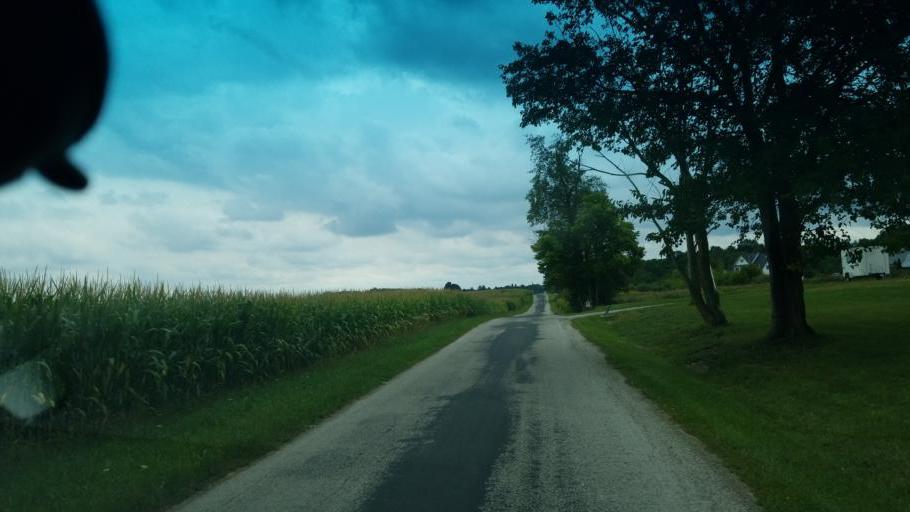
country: US
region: Ohio
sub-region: Richland County
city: Shelby
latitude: 40.8914
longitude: -82.5714
